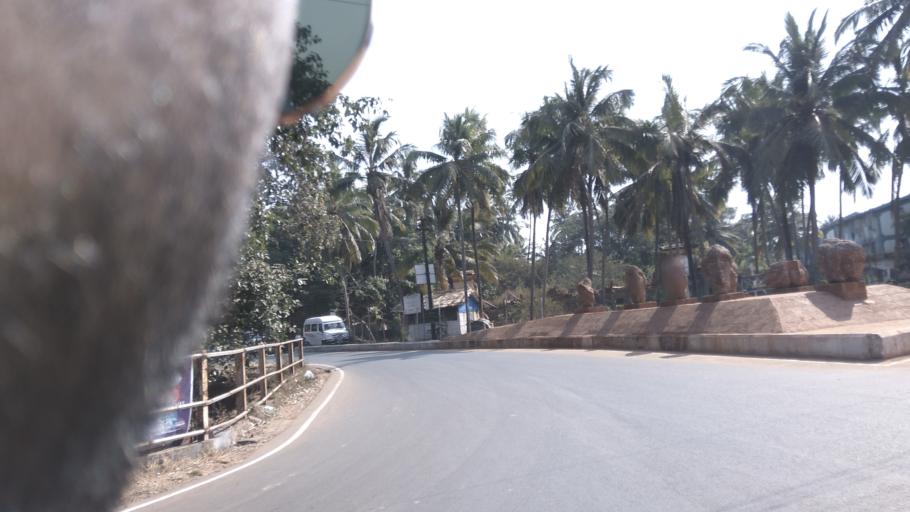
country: IN
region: Goa
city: Calangute
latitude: 15.5369
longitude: 73.7644
